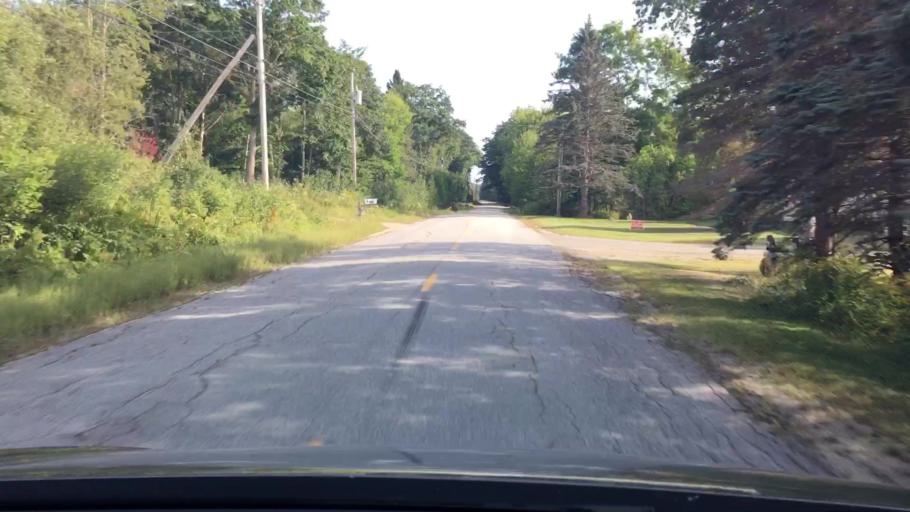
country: US
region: Maine
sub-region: Hancock County
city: Bucksport
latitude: 44.5417
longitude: -68.7957
